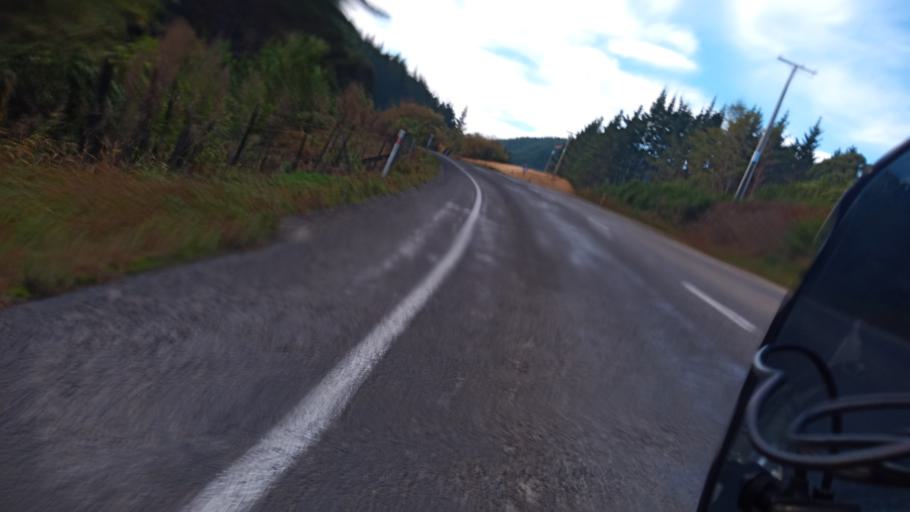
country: NZ
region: Gisborne
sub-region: Gisborne District
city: Gisborne
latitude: -38.8360
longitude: 177.8948
